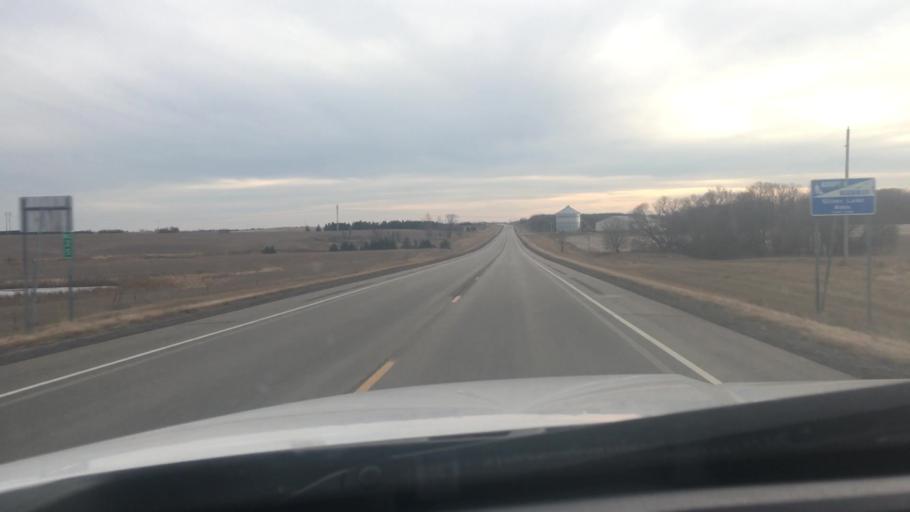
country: US
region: Minnesota
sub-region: Otter Tail County
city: Perham
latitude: 46.3242
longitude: -95.7185
